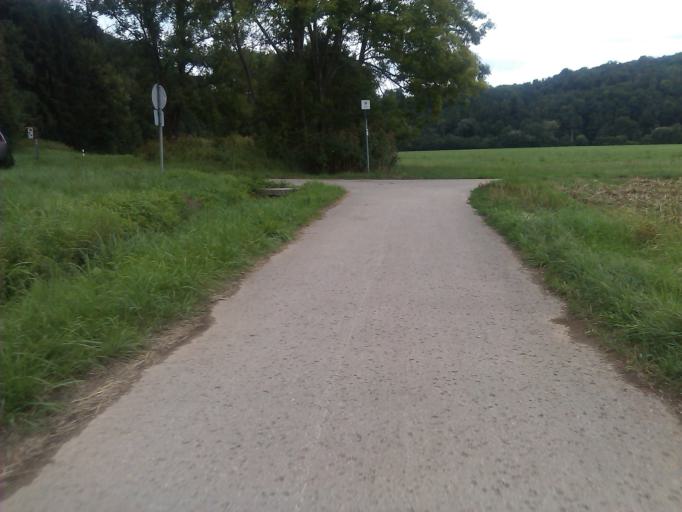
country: DE
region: Baden-Wuerttemberg
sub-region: Regierungsbezirk Stuttgart
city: Neckartenzlingen
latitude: 48.5757
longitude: 9.2288
